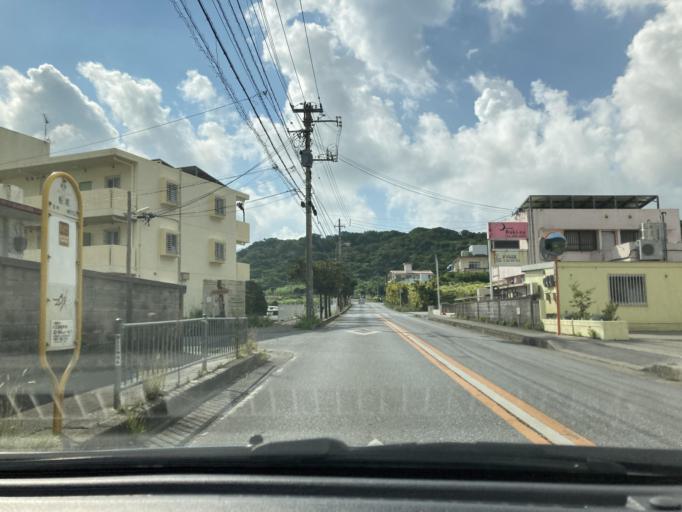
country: JP
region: Okinawa
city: Tomigusuku
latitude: 26.1515
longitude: 127.7522
